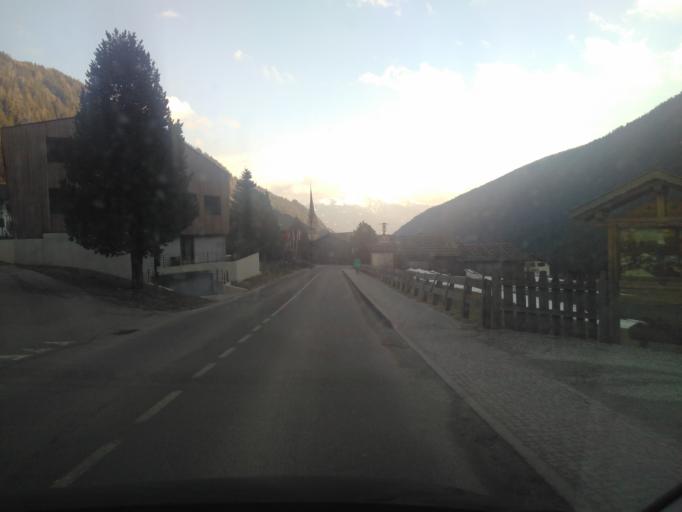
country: IT
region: Trentino-Alto Adige
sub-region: Bolzano
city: Fortezza
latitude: 46.8418
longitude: 11.6250
